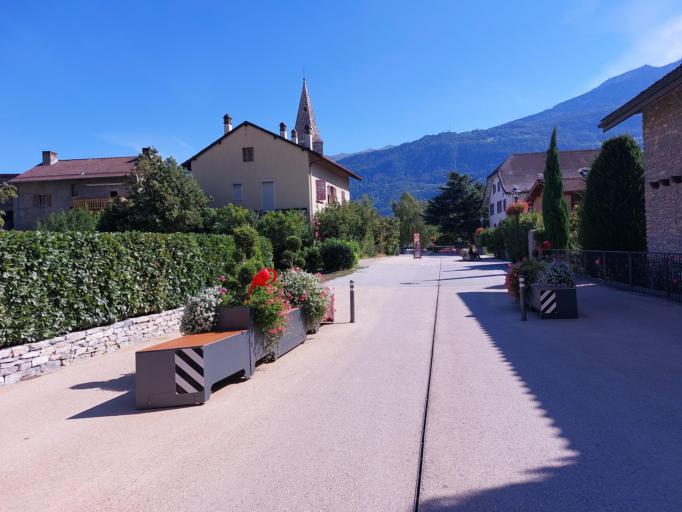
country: CH
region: Valais
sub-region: Conthey District
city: Ardon
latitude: 46.2105
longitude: 7.2555
